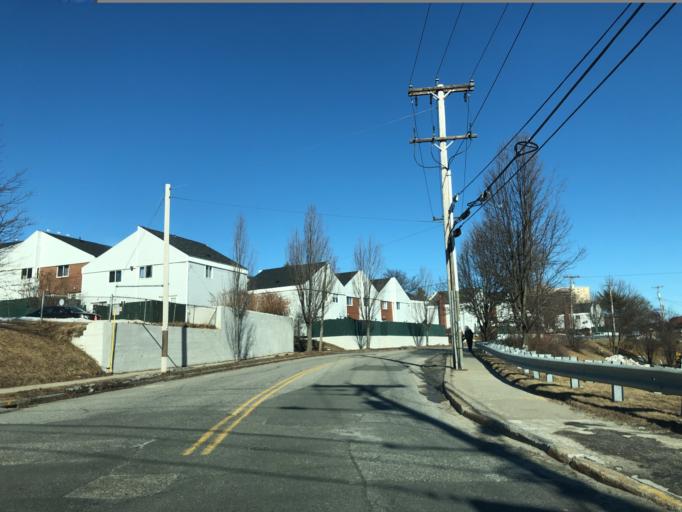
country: US
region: Maine
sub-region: Cumberland County
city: Portland
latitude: 43.6616
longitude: -70.2475
